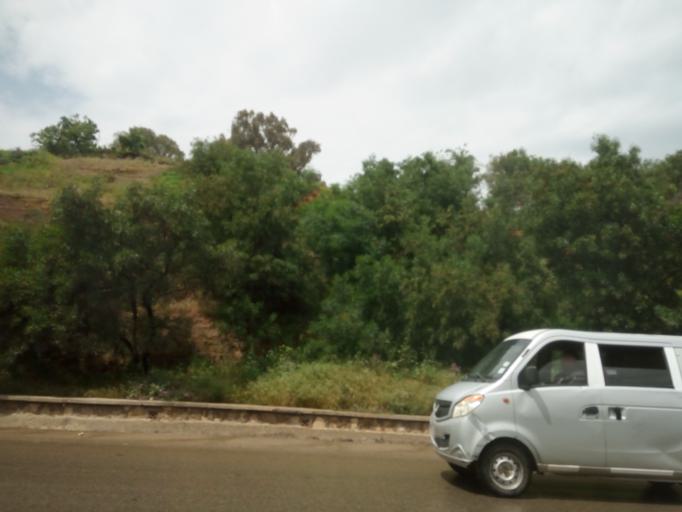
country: DZ
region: Alger
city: Bab Ezzouar
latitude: 36.7323
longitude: 3.1190
